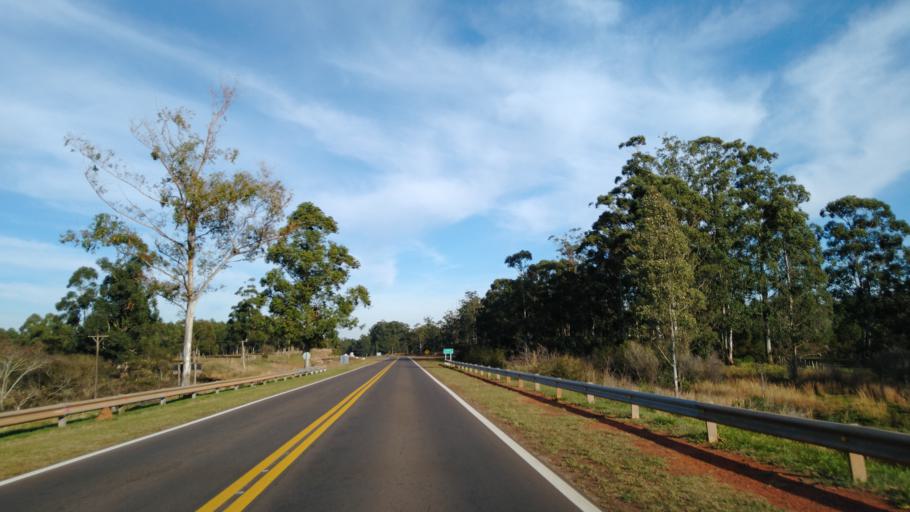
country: AR
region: Corrientes
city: Yapeyu
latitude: -29.4239
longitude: -56.8560
